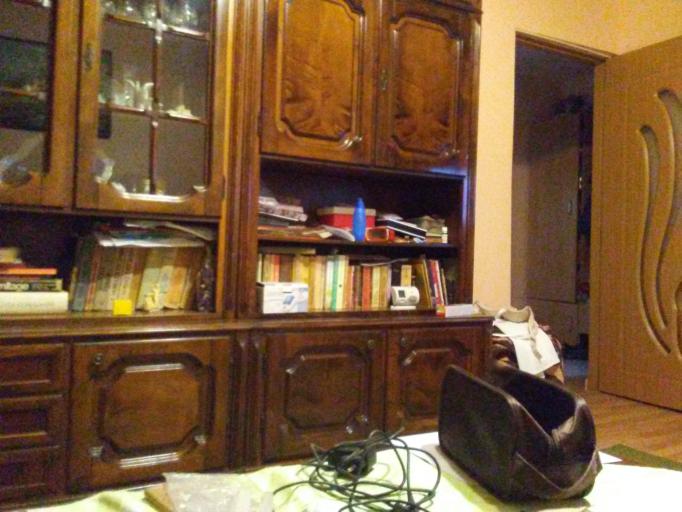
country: RO
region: Maramures
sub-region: Municipiul Sighetu Marmatiei
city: Sighetu Marmatiei
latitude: 47.9269
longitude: 23.9042
